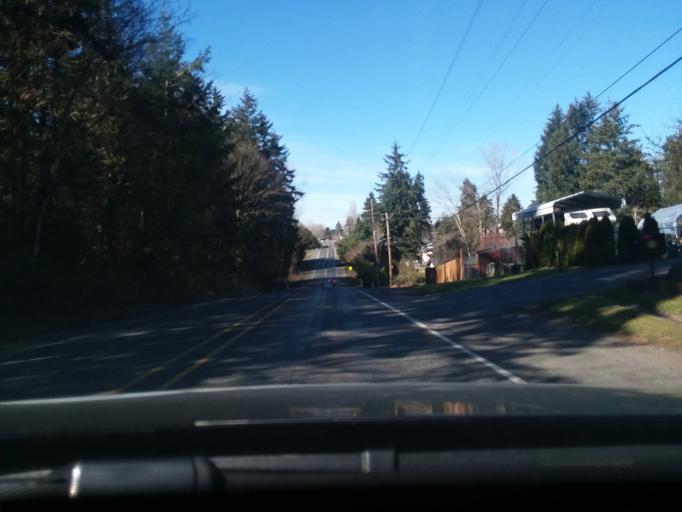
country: US
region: Washington
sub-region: Pierce County
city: Summit
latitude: 47.1619
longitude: -122.3471
